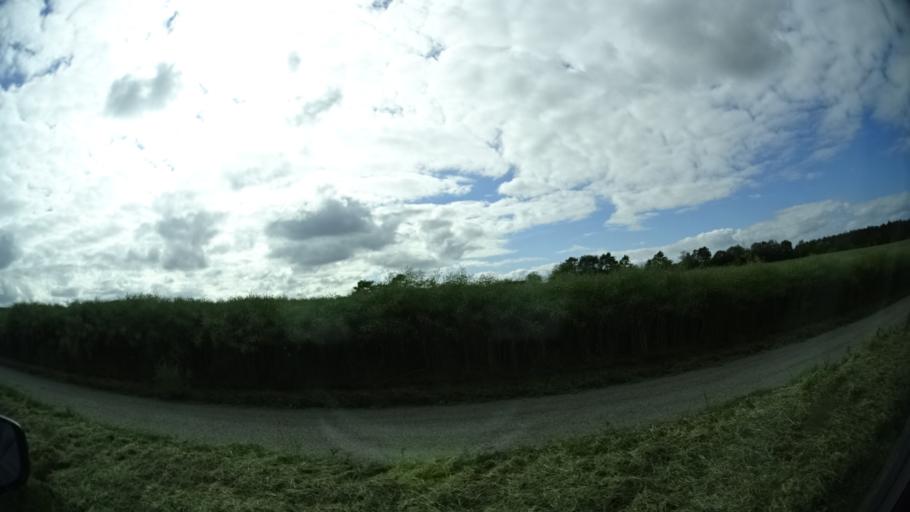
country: DK
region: Central Jutland
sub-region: Norddjurs Kommune
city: Grenaa
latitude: 56.4807
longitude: 10.7290
